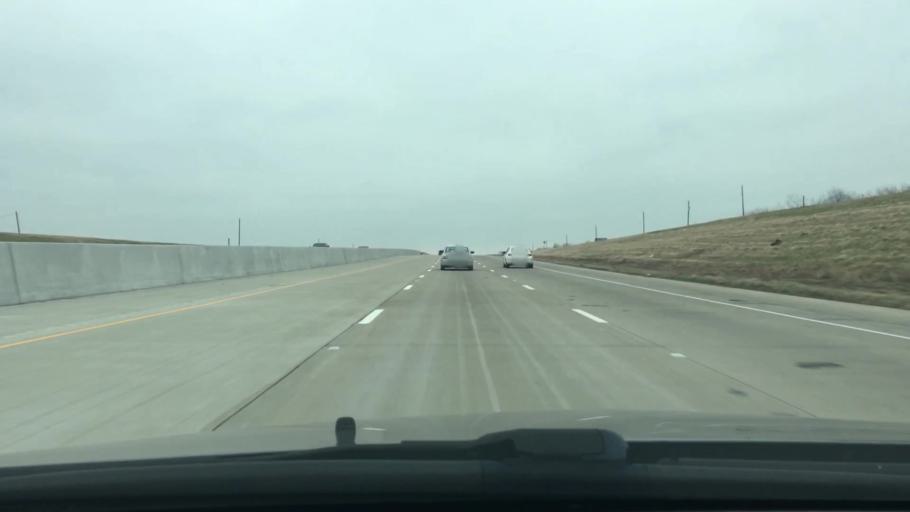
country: US
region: Texas
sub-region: Freestone County
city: Wortham
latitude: 31.9043
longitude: -96.3828
